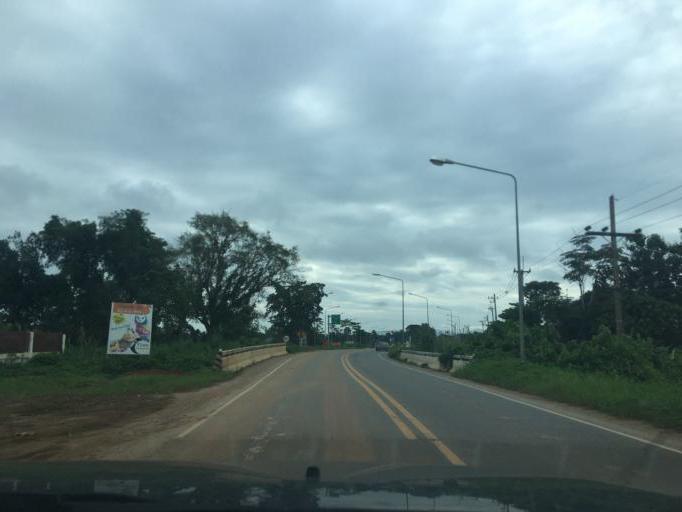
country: TH
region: Chiang Rai
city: Chiang Rai
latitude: 20.0052
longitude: 99.8905
